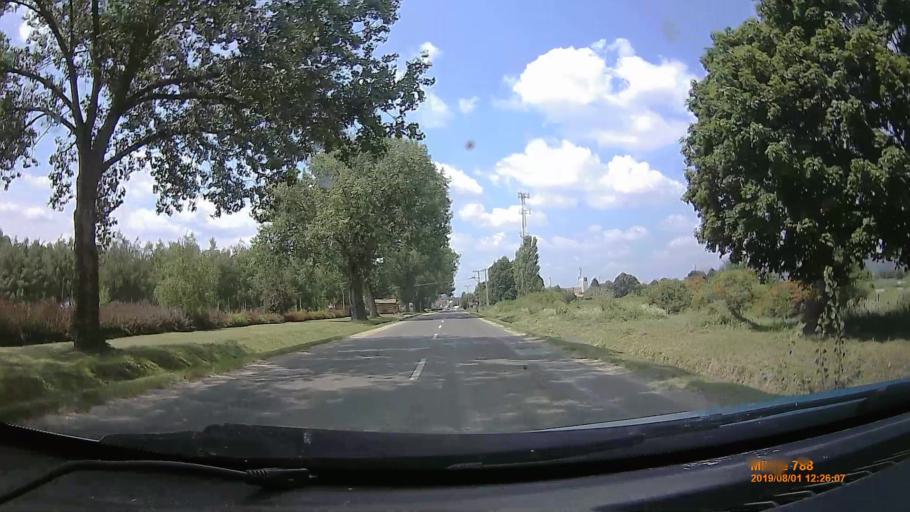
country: HU
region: Baranya
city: Siklos
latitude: 45.8518
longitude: 18.3160
